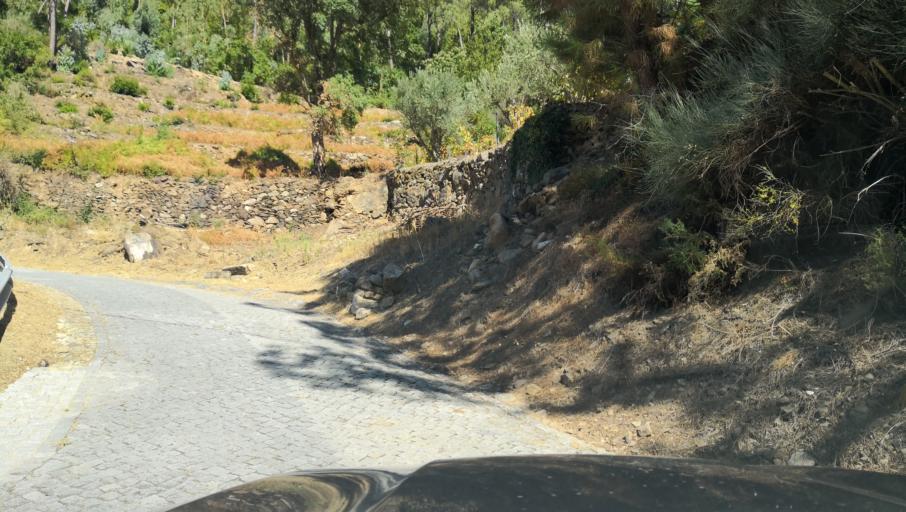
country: PT
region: Vila Real
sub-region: Santa Marta de Penaguiao
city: Santa Marta de Penaguiao
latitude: 41.2540
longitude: -7.8150
